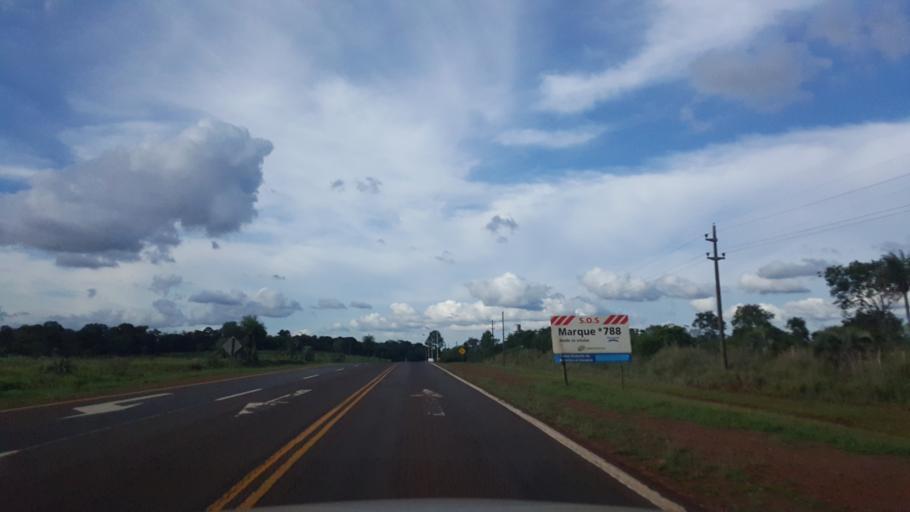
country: AR
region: Misiones
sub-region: Departamento de Candelaria
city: Loreto
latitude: -27.3387
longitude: -55.5450
